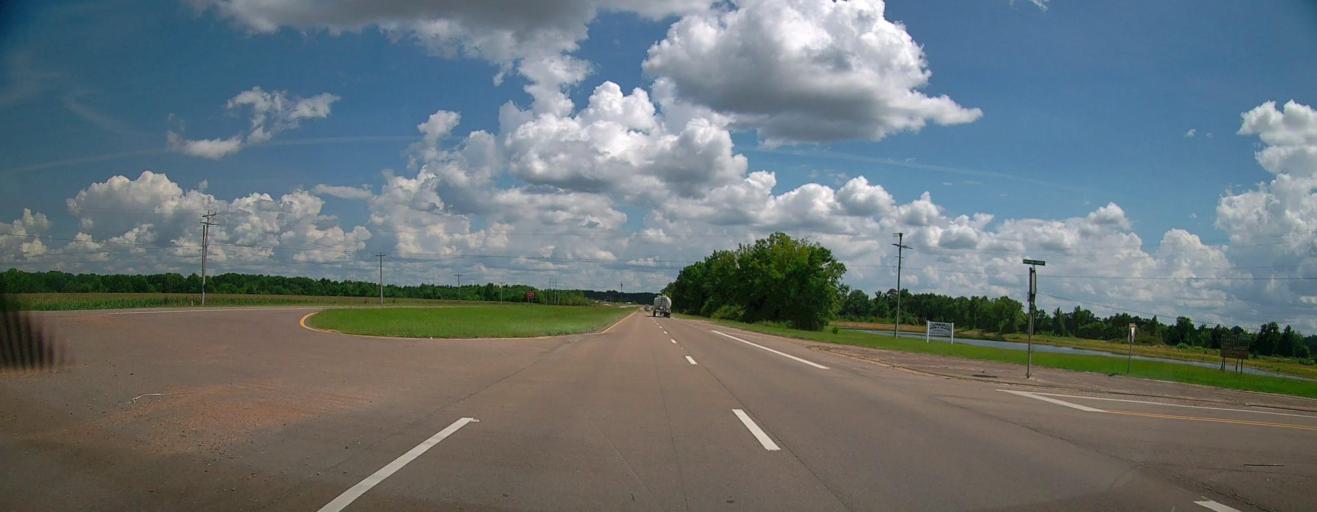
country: US
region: Mississippi
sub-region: Lowndes County
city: Columbus Air Force Base
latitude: 33.6655
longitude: -88.4246
